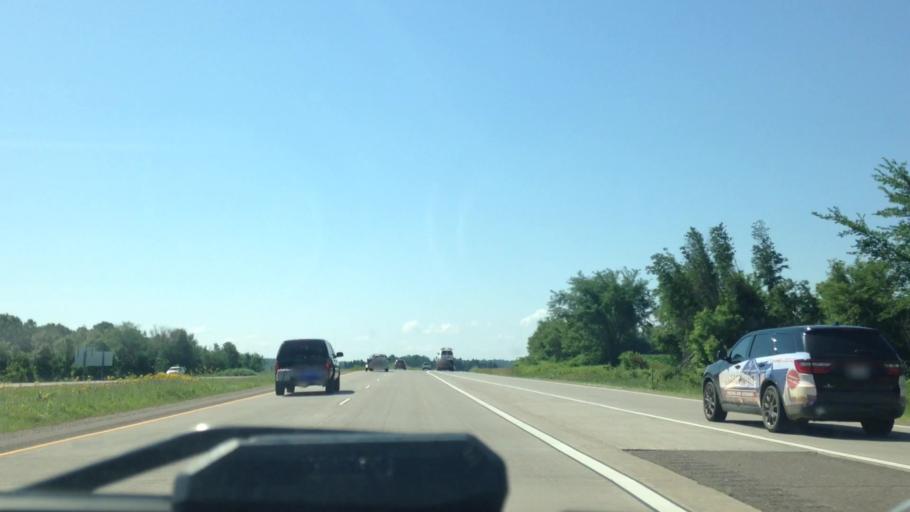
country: US
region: Wisconsin
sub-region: Barron County
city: Rice Lake
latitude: 45.4695
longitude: -91.7583
